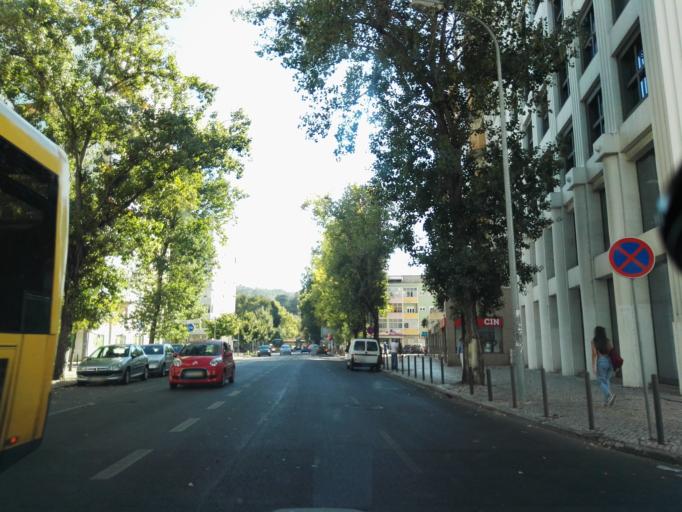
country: PT
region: Lisbon
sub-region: Odivelas
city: Pontinha
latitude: 38.7505
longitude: -9.1913
